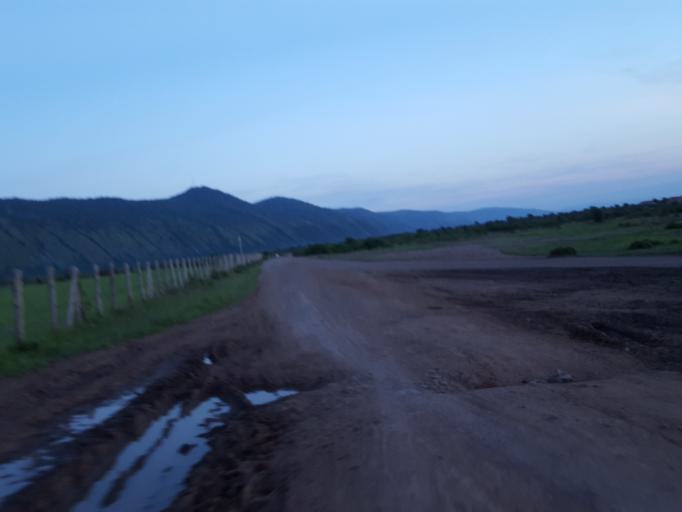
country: UG
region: Western Region
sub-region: Kibale District
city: Kagadi
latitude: 1.2423
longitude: 30.7468
